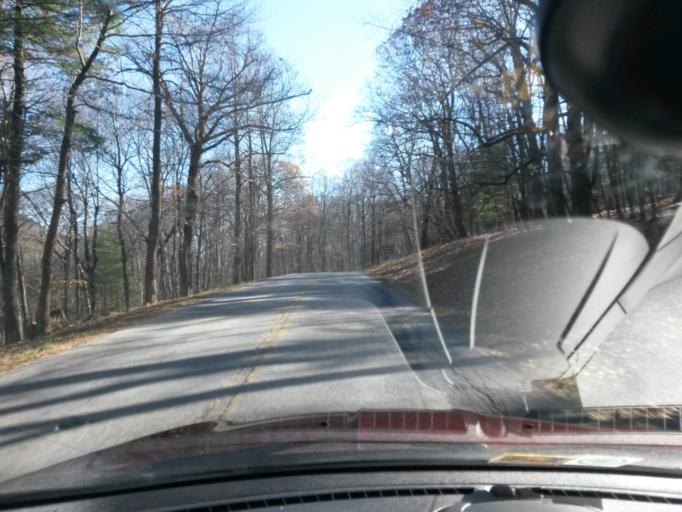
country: US
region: Virginia
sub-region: Botetourt County
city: Buchanan
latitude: 37.4440
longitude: -79.6063
